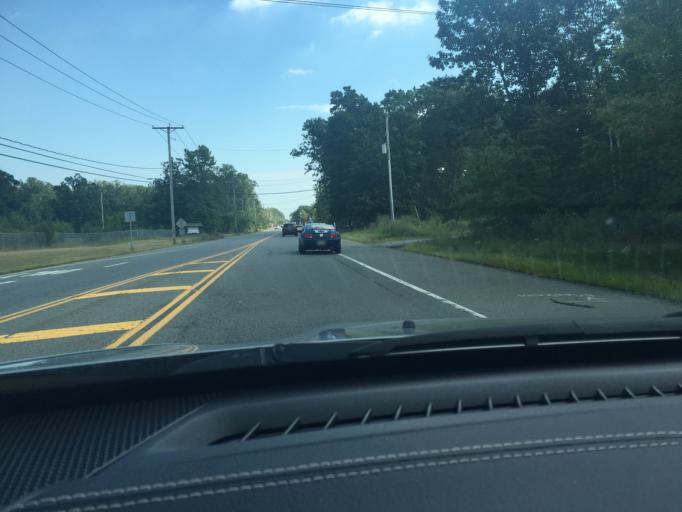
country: US
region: New Jersey
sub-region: Ocean County
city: Leisure Knoll
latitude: 40.0263
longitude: -74.2743
